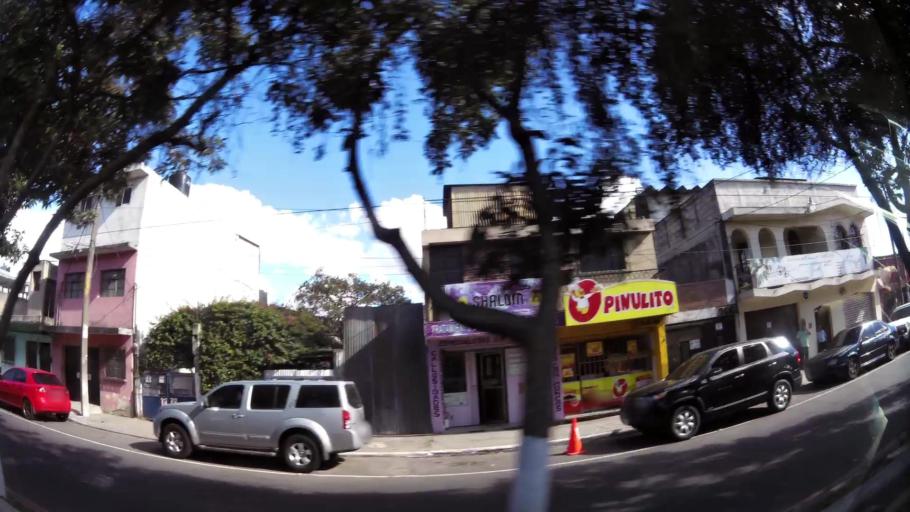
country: GT
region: Guatemala
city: Guatemala City
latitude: 14.6201
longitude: -90.5481
